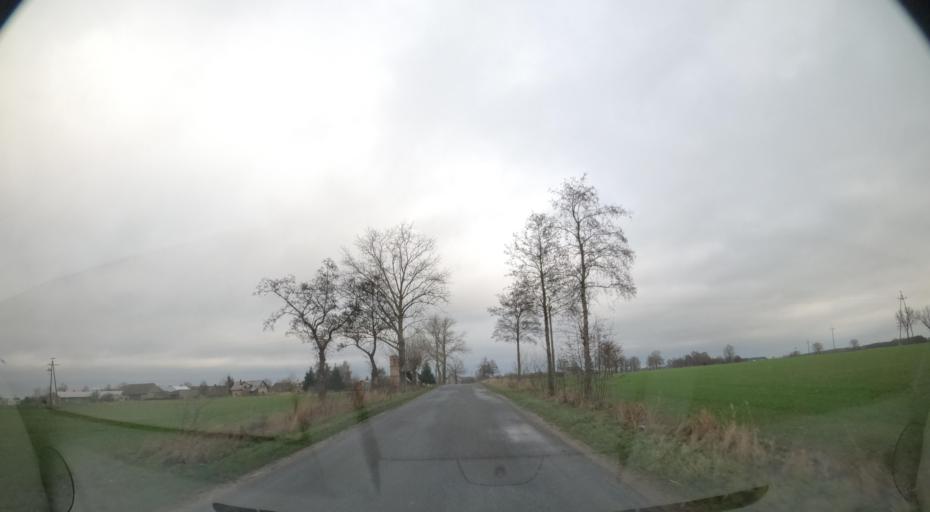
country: PL
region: Greater Poland Voivodeship
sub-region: Powiat pilski
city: Wysoka
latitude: 53.2558
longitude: 17.1522
